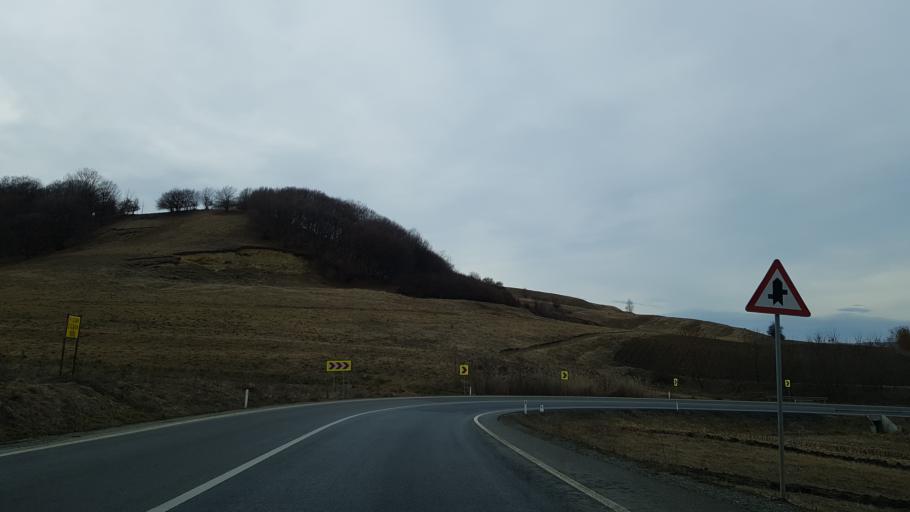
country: RO
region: Sibiu
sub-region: Comuna Slimnic
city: Slimnic
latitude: 45.9504
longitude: 24.1710
